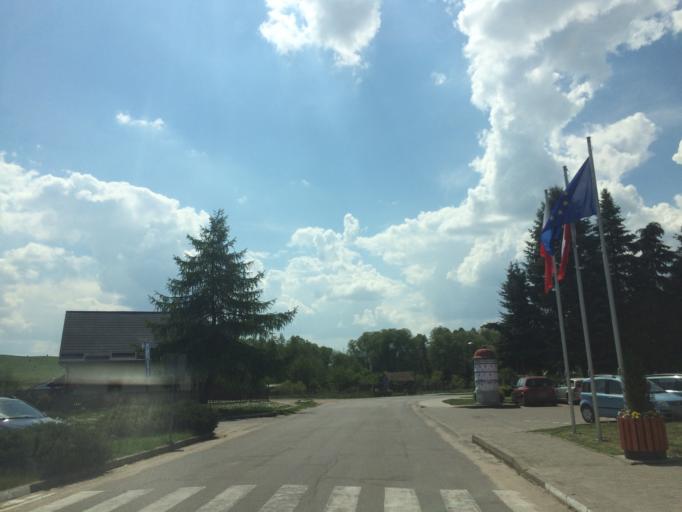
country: PL
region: Warmian-Masurian Voivodeship
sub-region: Powiat nowomiejski
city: Nowe Miasto Lubawskie
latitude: 53.4416
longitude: 19.6066
